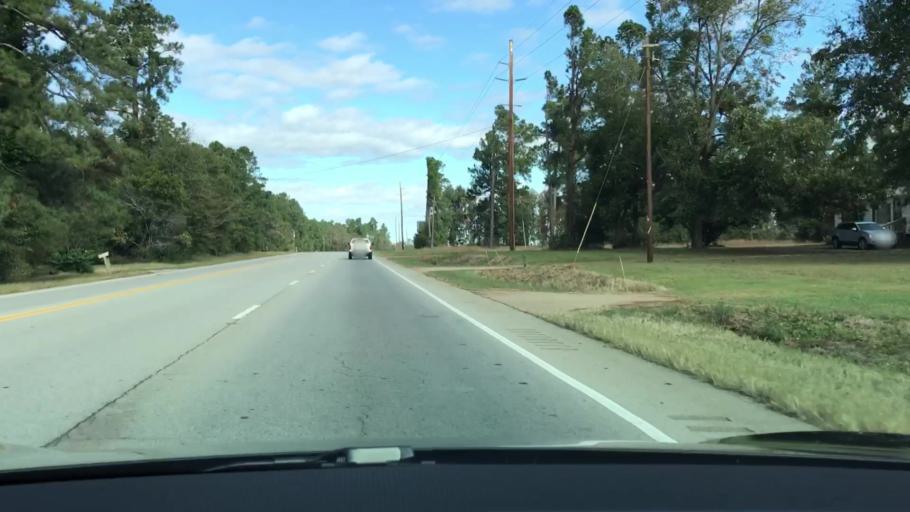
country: US
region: Georgia
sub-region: Jefferson County
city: Louisville
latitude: 33.0327
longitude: -82.4053
